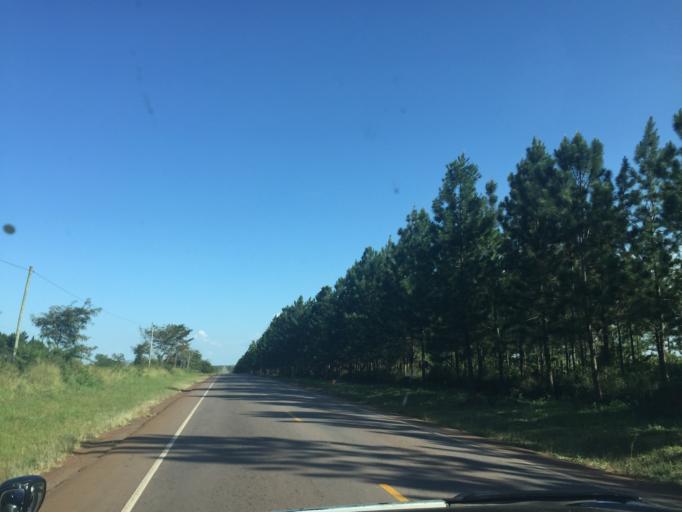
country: UG
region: Central Region
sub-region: Nakasongola District
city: Nakasongola
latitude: 1.3765
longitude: 32.3448
